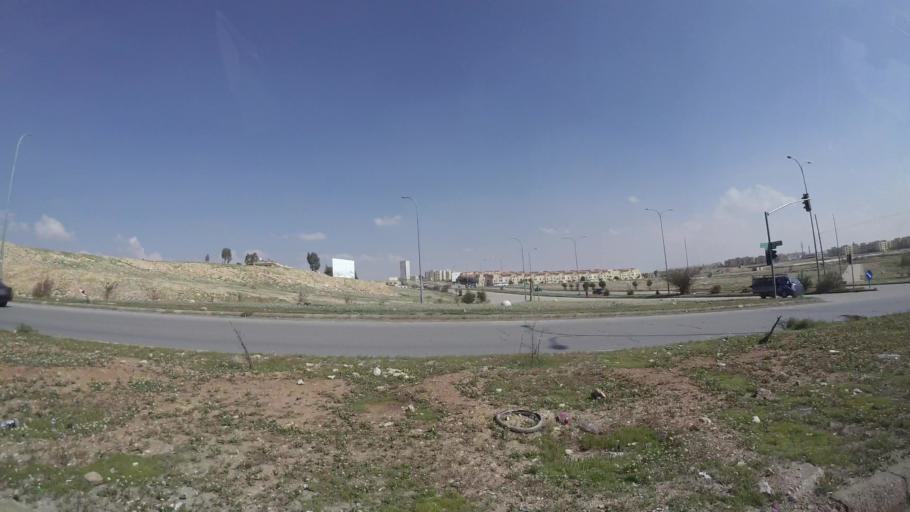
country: JO
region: Zarqa
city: Zarqa
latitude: 32.0731
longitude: 36.1040
